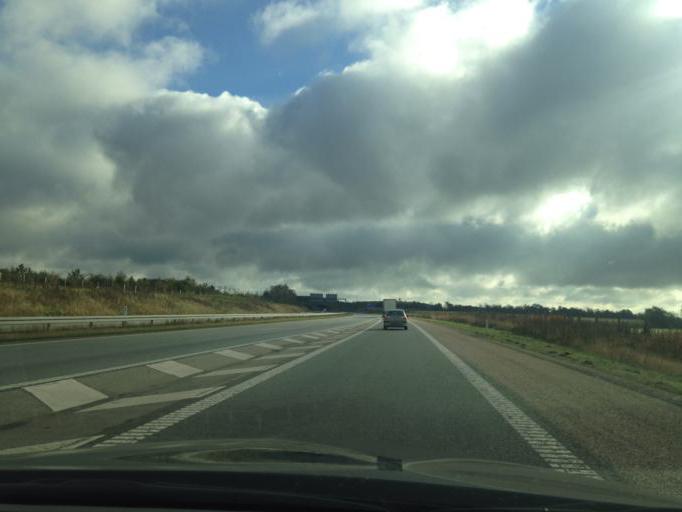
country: DK
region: South Denmark
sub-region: Vejle Kommune
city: Give
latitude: 55.8402
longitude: 9.2794
